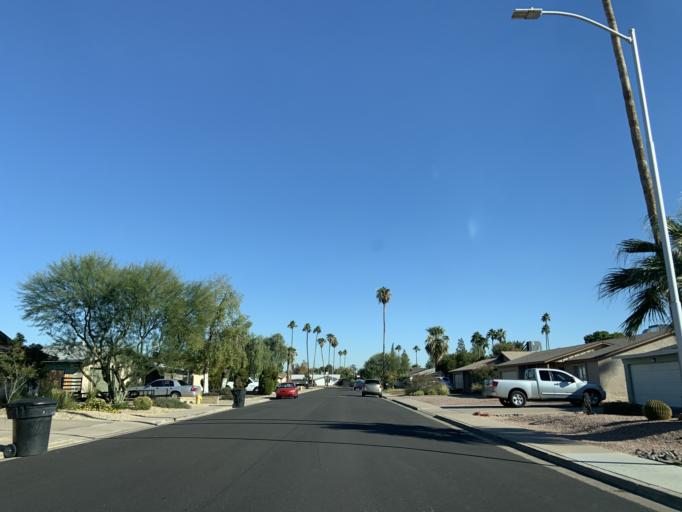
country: US
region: Arizona
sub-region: Maricopa County
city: Tempe
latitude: 33.3989
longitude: -111.8792
